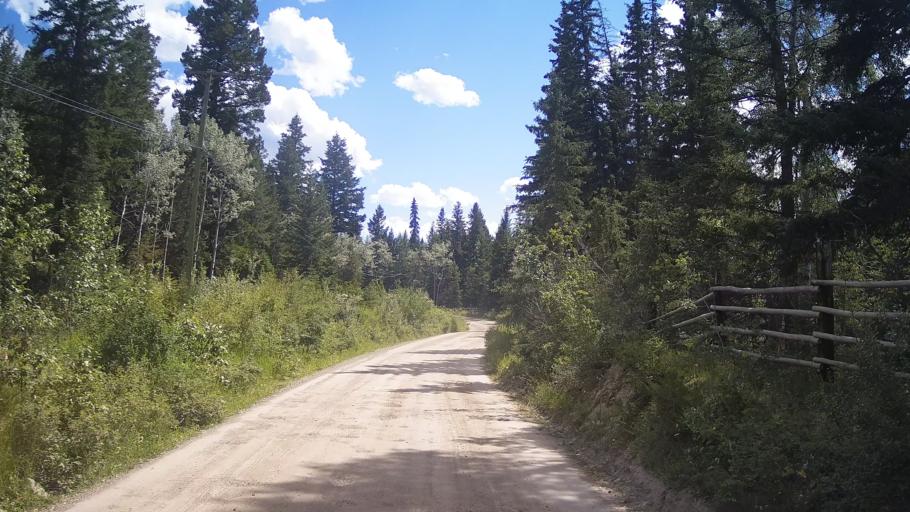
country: CA
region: British Columbia
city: Lillooet
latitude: 51.2816
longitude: -121.9675
